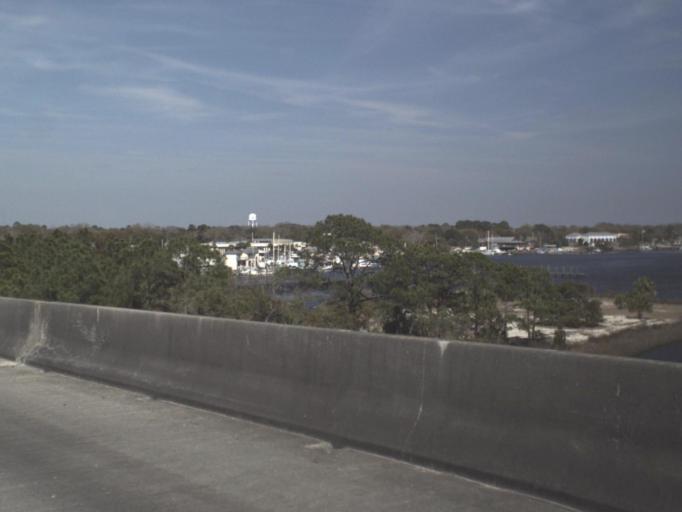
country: US
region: Florida
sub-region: Franklin County
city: Carrabelle
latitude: 29.8495
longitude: -84.6767
